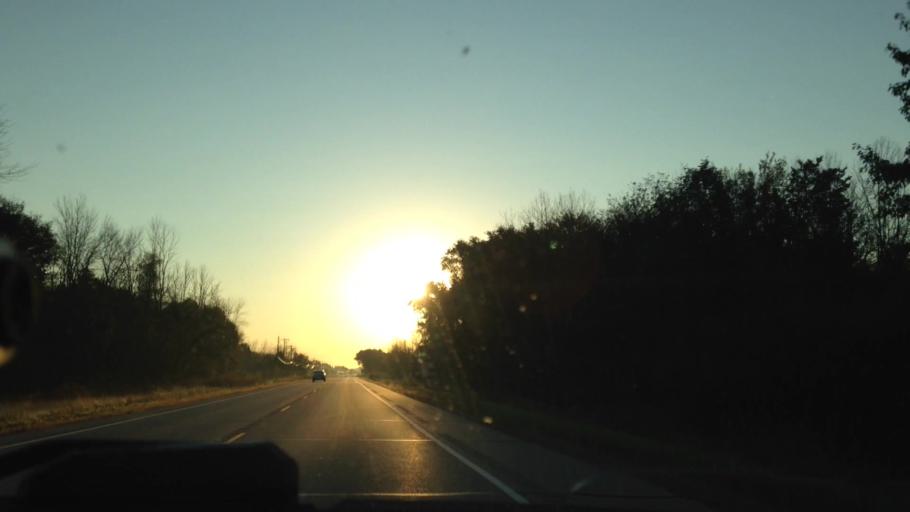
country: US
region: Wisconsin
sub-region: Washington County
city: West Bend
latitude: 43.4259
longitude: -88.1150
